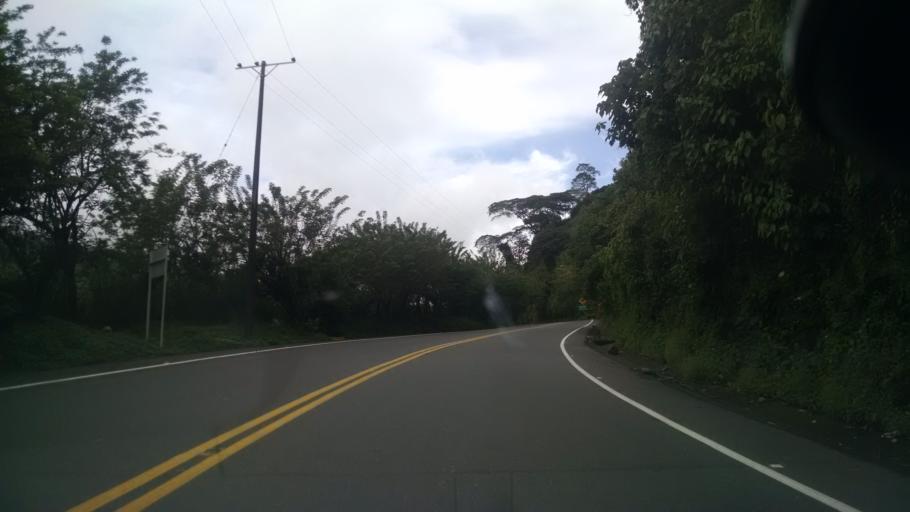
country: CO
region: Caldas
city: Palestina
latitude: 5.0510
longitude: -75.6023
